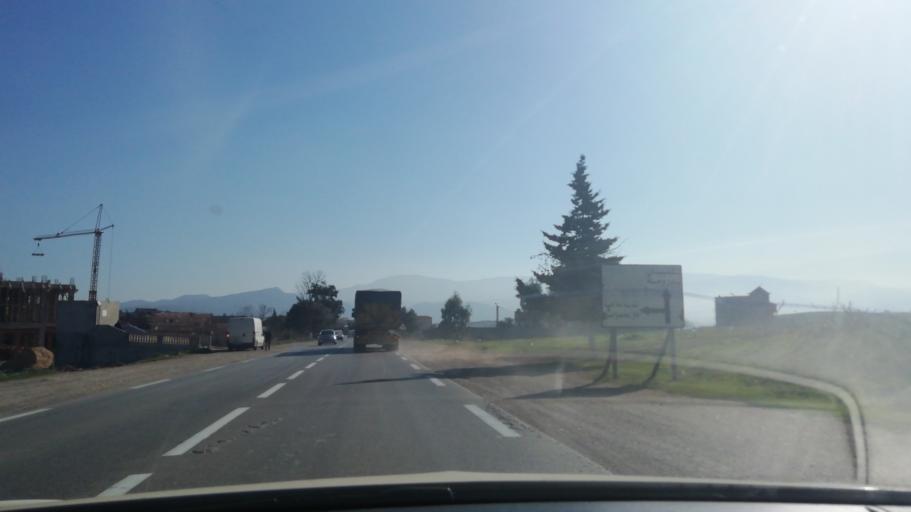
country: DZ
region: Tlemcen
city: Nedroma
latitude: 35.0783
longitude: -1.7889
